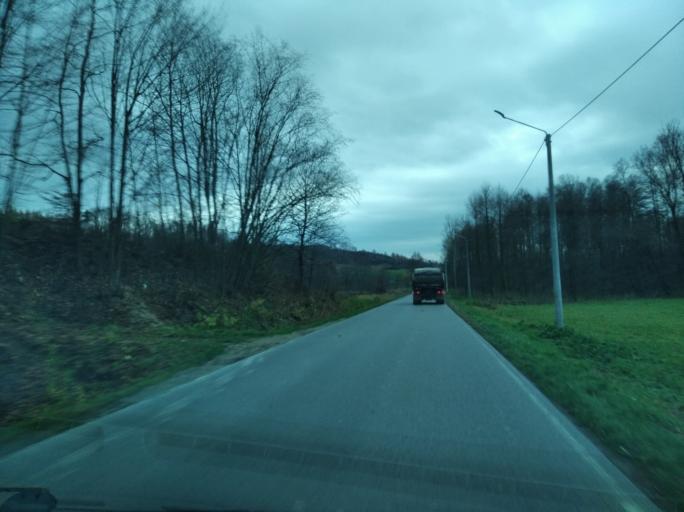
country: PL
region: Subcarpathian Voivodeship
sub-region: Powiat strzyzowski
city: Wisniowa
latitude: 49.9239
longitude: 21.7168
